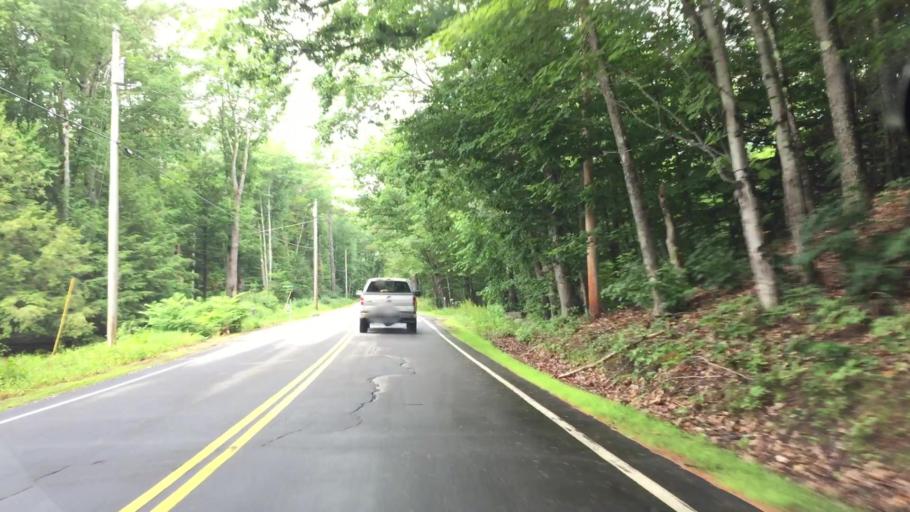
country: US
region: New Hampshire
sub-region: Carroll County
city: Sandwich
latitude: 43.8048
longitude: -71.4644
